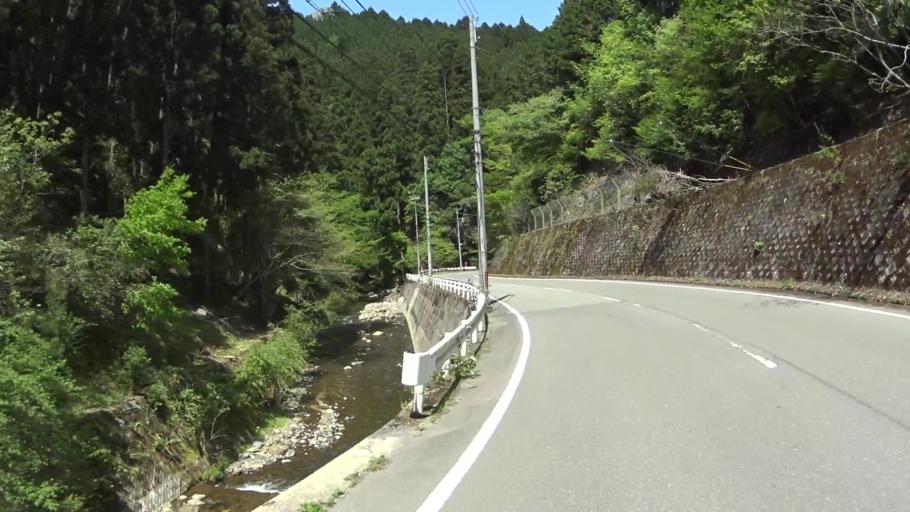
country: JP
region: Shiga Prefecture
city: Kitahama
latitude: 35.2001
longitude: 135.7856
